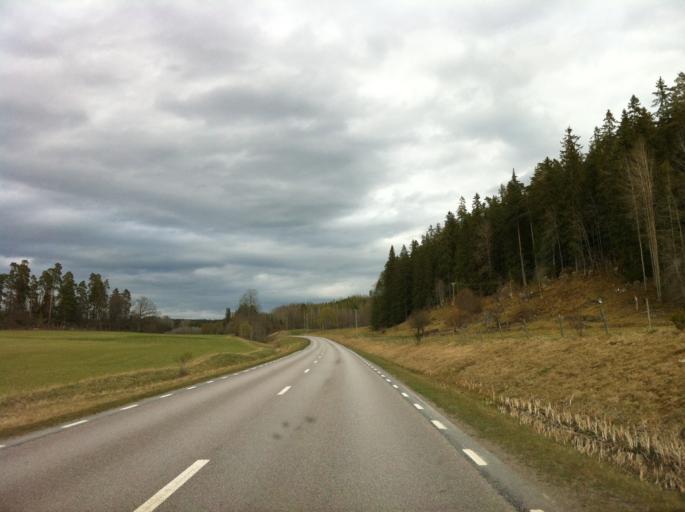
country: SE
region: OEstergoetland
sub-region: Kinda Kommun
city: Rimforsa
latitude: 58.0785
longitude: 15.8255
